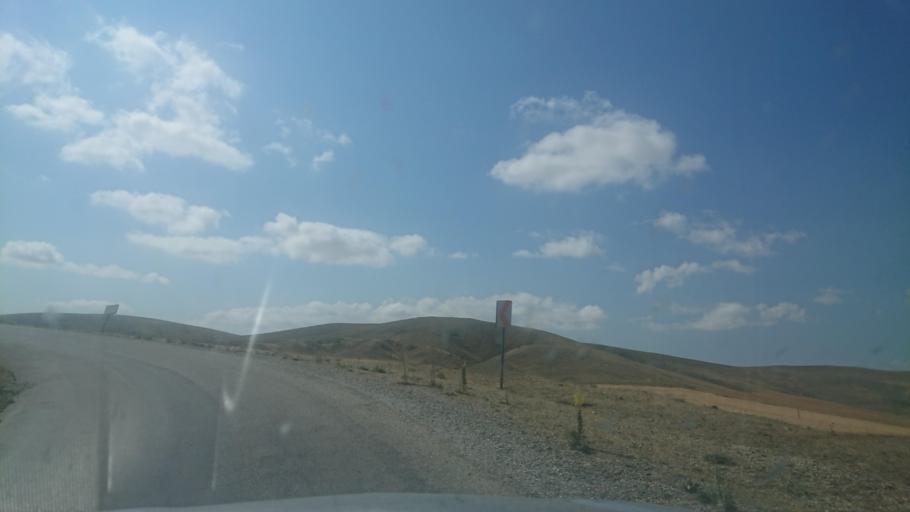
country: TR
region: Aksaray
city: Sariyahsi
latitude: 39.0059
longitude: 33.9573
